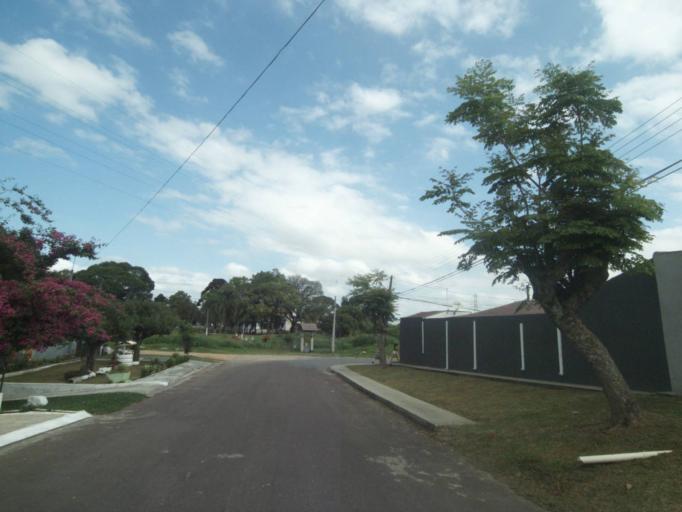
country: BR
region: Parana
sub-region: Pinhais
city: Pinhais
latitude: -25.4084
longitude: -49.1966
